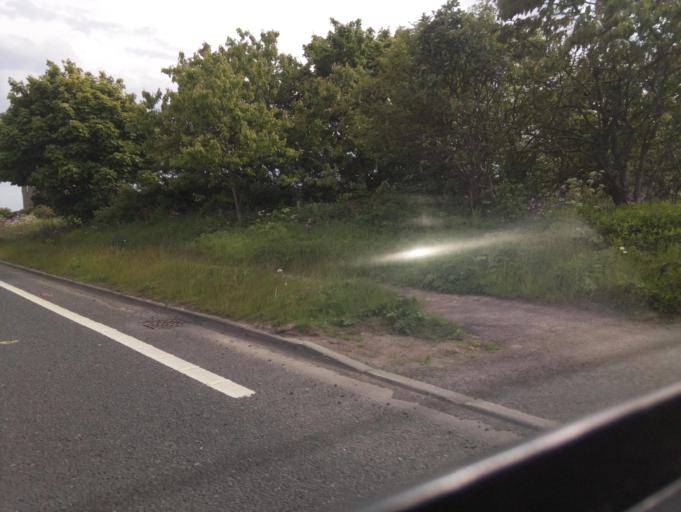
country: GB
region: England
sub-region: Northumberland
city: Berwick-Upon-Tweed
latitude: 55.7882
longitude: -2.0199
